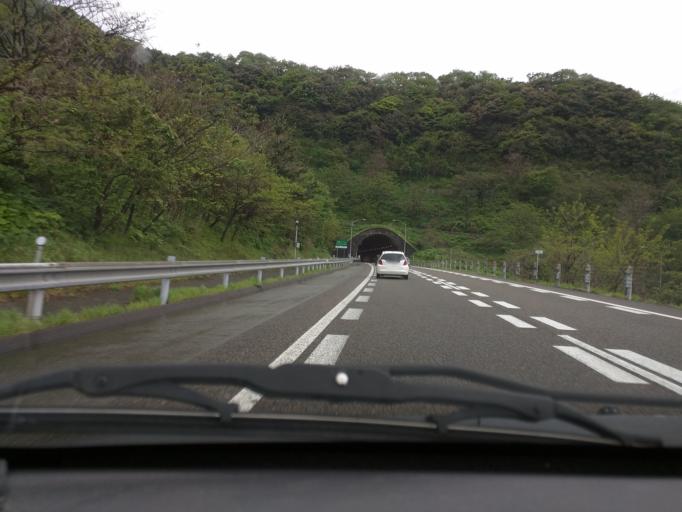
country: JP
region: Niigata
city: Kashiwazaki
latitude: 37.3033
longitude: 138.4185
